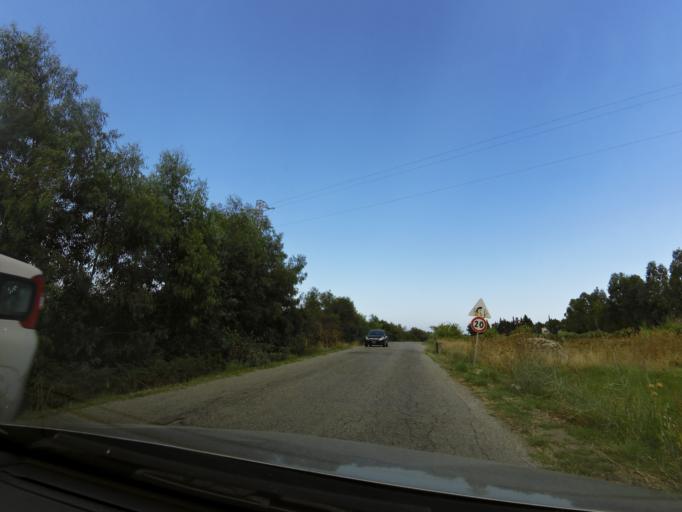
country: IT
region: Calabria
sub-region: Provincia di Reggio Calabria
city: Monasterace Marina
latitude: 38.4218
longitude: 16.5547
